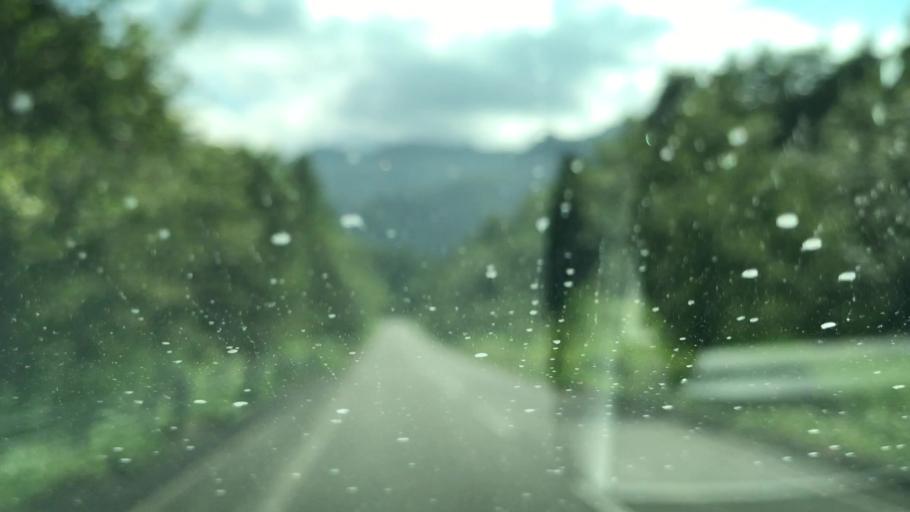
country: JP
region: Hokkaido
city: Shimo-furano
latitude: 42.8496
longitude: 142.4297
